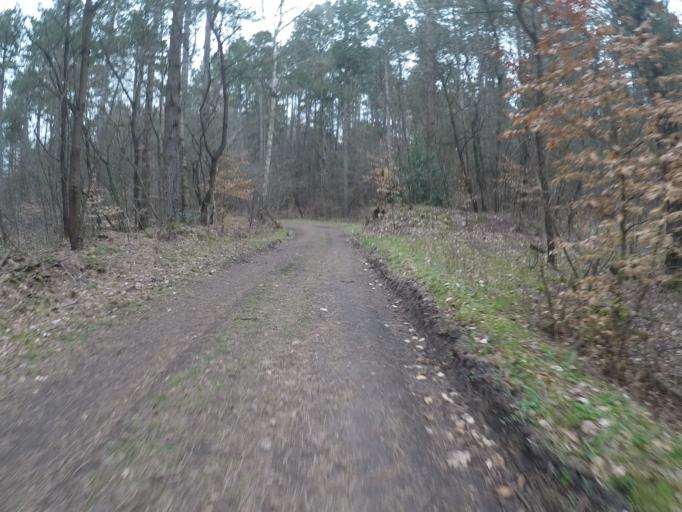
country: DE
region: Lower Saxony
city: Nordholz
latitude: 53.8195
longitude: 8.6440
